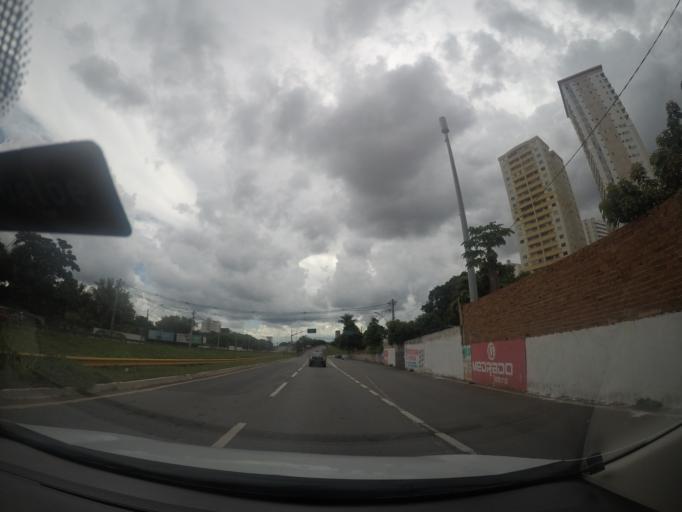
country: BR
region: Goias
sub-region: Goiania
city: Goiania
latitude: -16.6976
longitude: -49.2446
